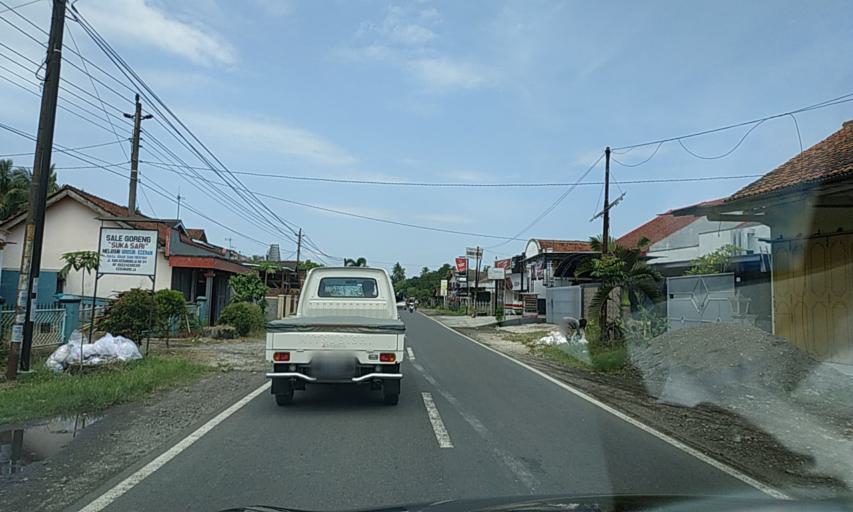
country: ID
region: Central Java
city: Mulyosari
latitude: -7.4973
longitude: 108.7890
